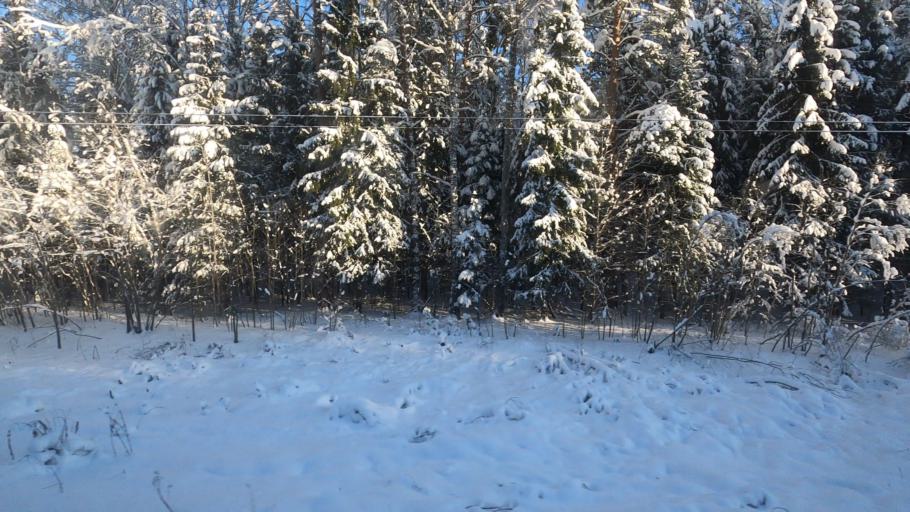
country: RU
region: Moskovskaya
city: Novo-Nikol'skoye
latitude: 56.6342
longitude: 37.5626
